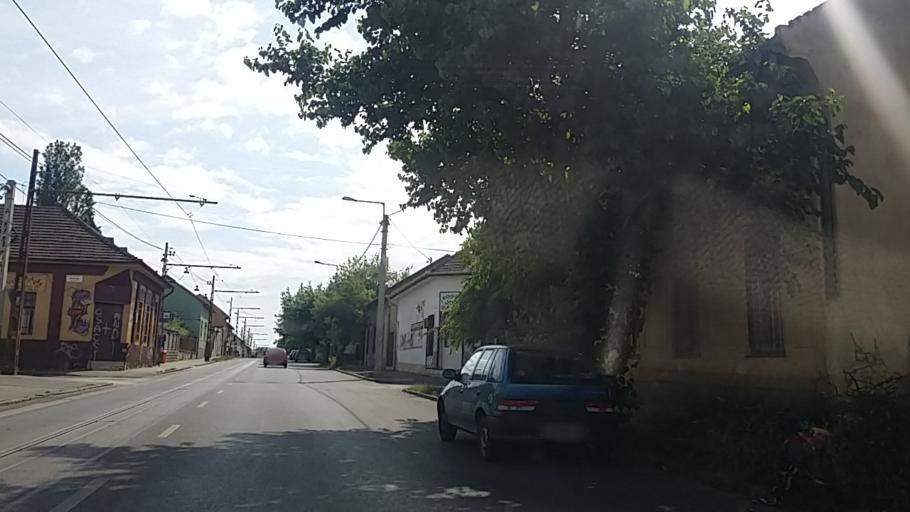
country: HU
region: Budapest
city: Budapest XX. keruelet
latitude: 47.4390
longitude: 19.1159
